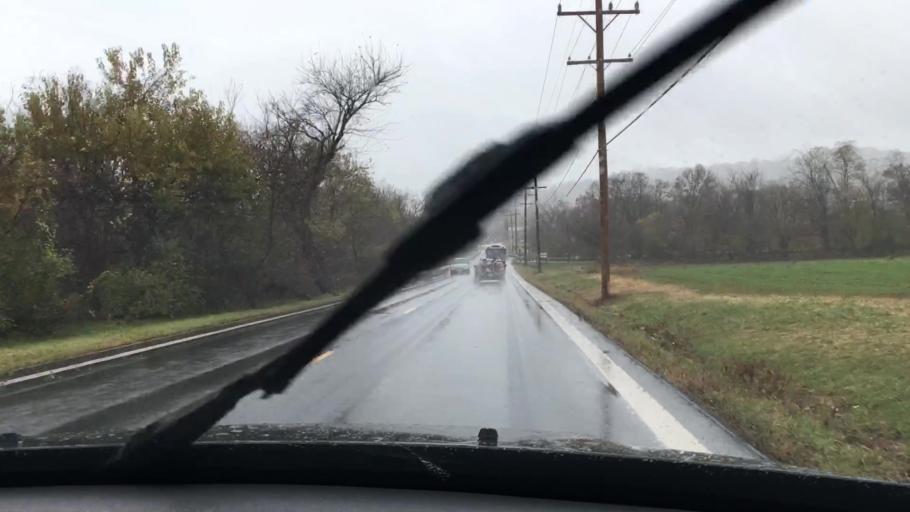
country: US
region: Maryland
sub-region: Frederick County
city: Point of Rocks
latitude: 39.2752
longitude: -77.5209
